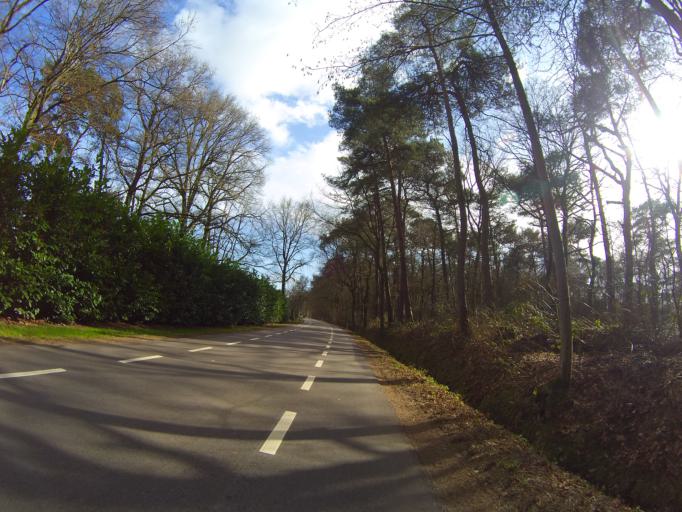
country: NL
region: Gelderland
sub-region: Gemeente Barneveld
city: Terschuur
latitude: 52.1536
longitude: 5.5250
